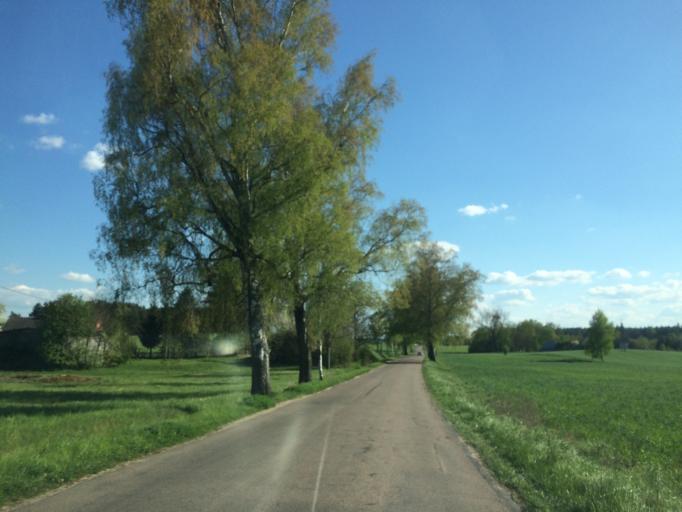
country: PL
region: Warmian-Masurian Voivodeship
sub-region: Powiat dzialdowski
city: Rybno
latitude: 53.4030
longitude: 19.9350
